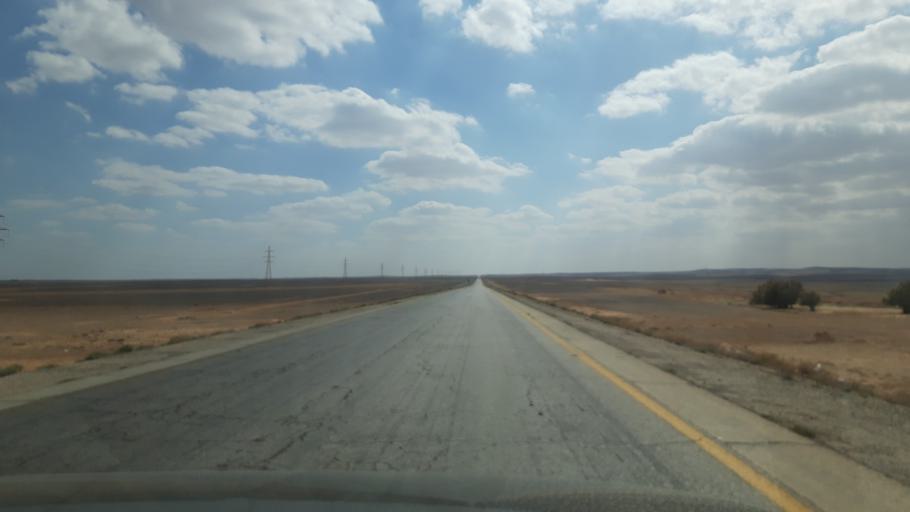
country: JO
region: Amman
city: Al Azraq ash Shamali
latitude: 31.7810
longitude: 36.5740
